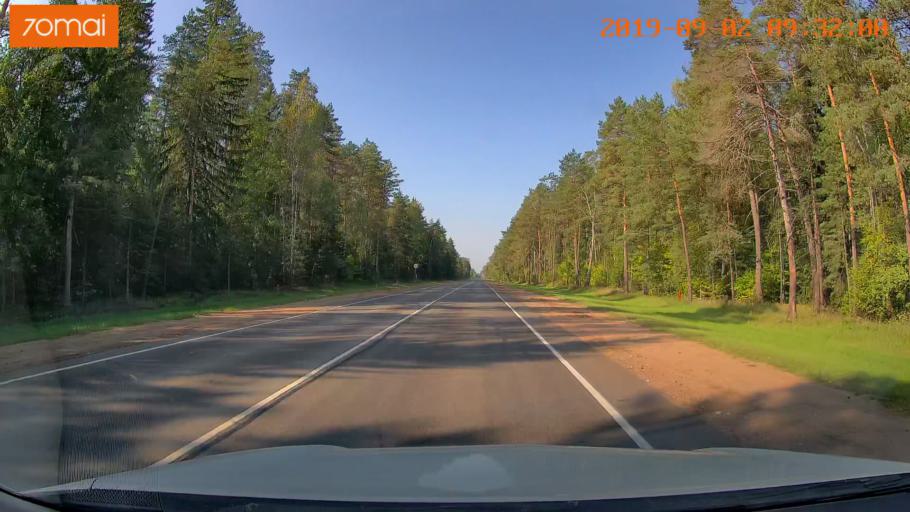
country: RU
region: Kaluga
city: Yukhnov
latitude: 54.7218
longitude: 35.1595
